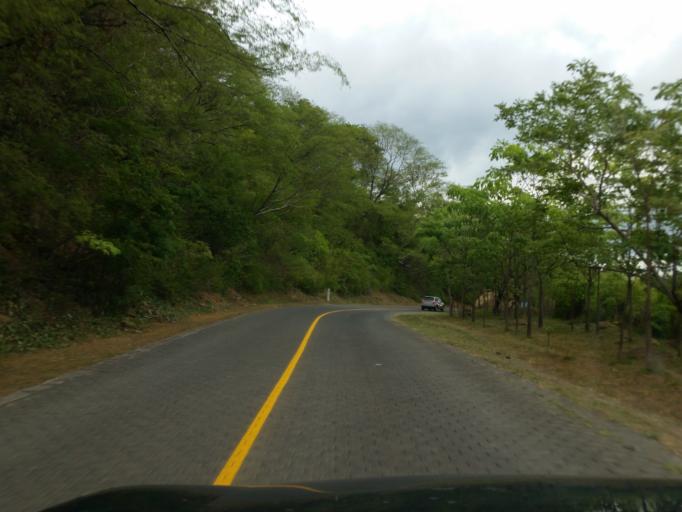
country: NI
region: Managua
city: Masachapa
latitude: 11.8634
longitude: -86.5176
